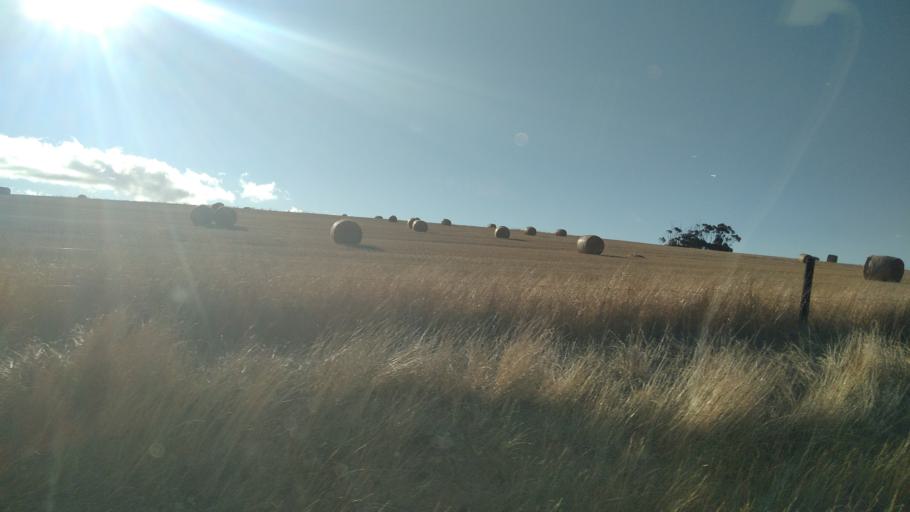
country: ZA
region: Western Cape
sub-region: Overberg District Municipality
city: Caledon
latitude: -34.1366
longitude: 19.2961
